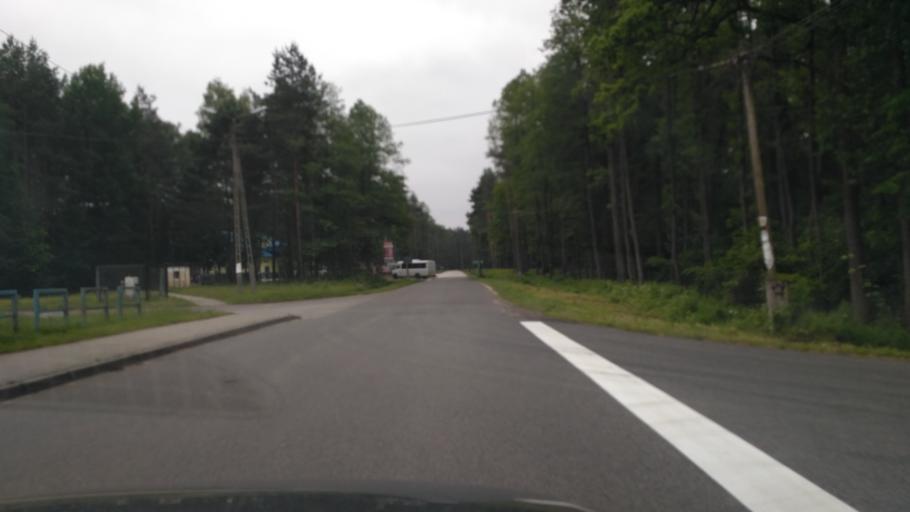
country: PL
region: Subcarpathian Voivodeship
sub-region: Powiat ropczycko-sedziszowski
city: Sedziszow Malopolski
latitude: 50.1335
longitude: 21.6698
